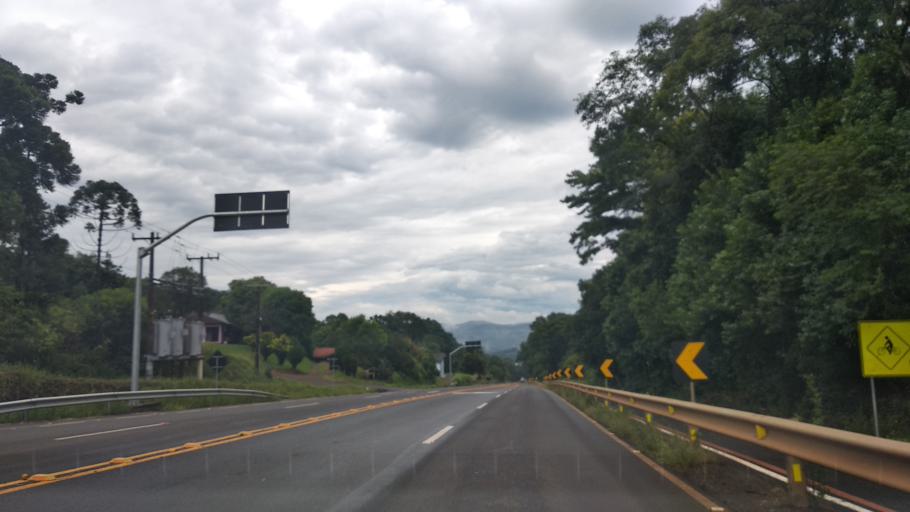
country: BR
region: Santa Catarina
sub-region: Videira
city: Videira
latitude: -27.0787
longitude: -51.2348
